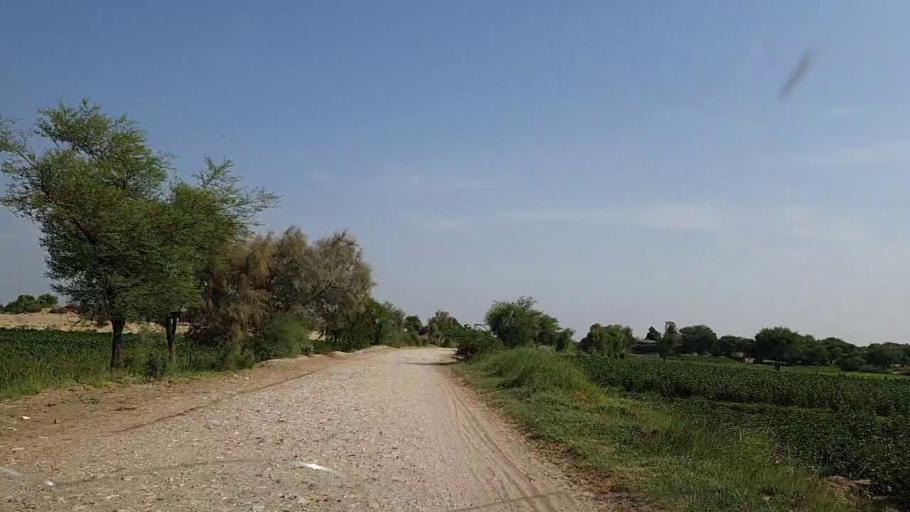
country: PK
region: Sindh
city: Khanpur
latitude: 27.7314
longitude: 69.3583
